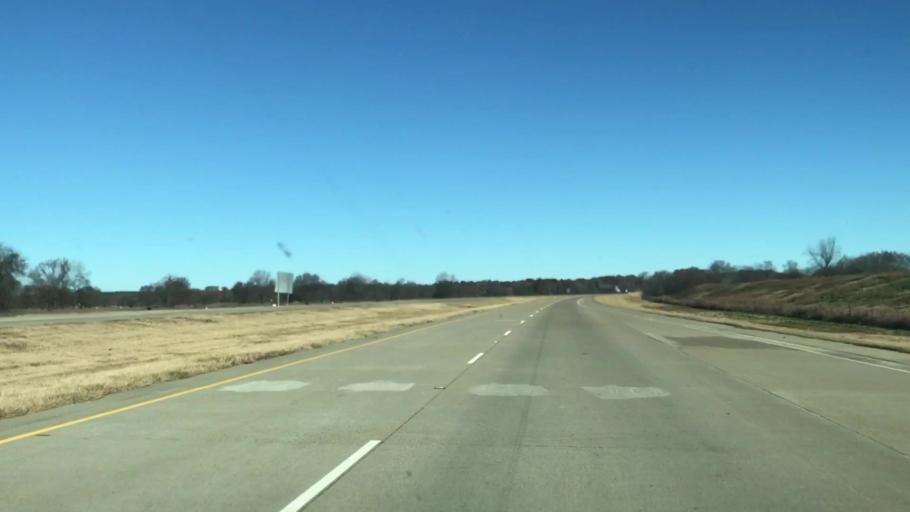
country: US
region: Louisiana
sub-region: Caddo Parish
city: Oil City
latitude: 32.7749
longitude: -93.8892
